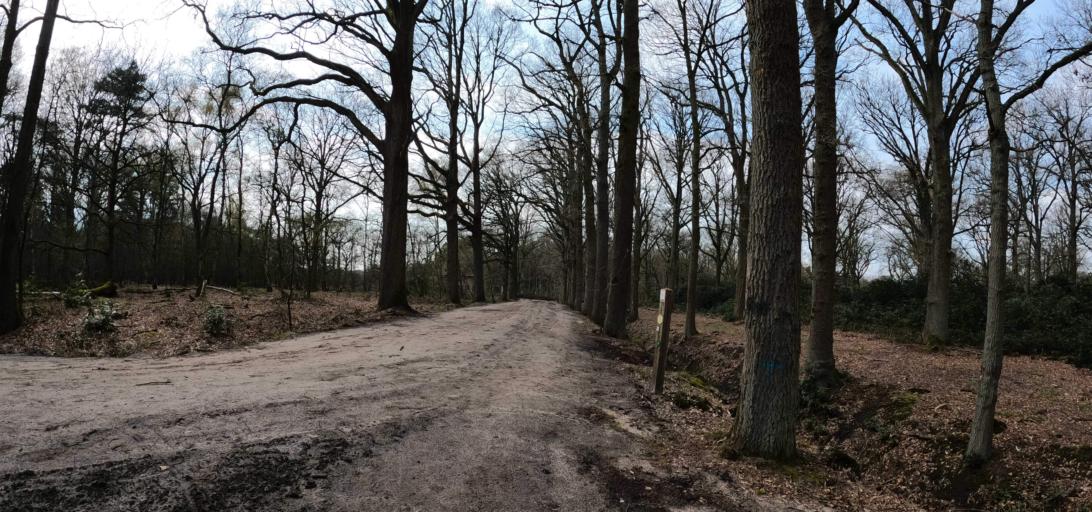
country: BE
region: Flanders
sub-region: Provincie Antwerpen
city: Kalmthout
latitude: 51.4190
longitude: 4.4417
